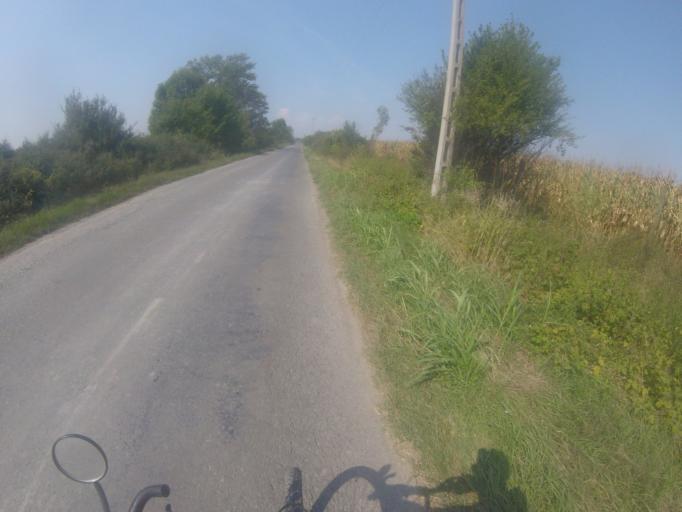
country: HU
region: Bacs-Kiskun
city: Ersekcsanad
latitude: 46.2564
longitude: 18.9420
